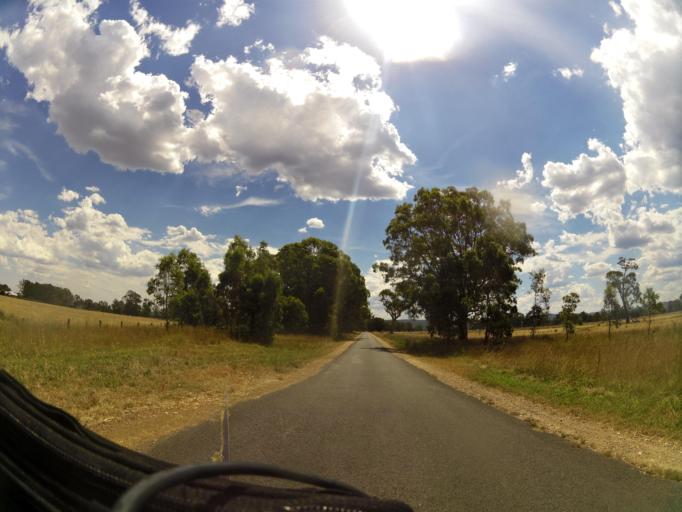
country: AU
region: Victoria
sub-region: Wellington
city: Heyfield
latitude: -37.9841
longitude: 146.7222
